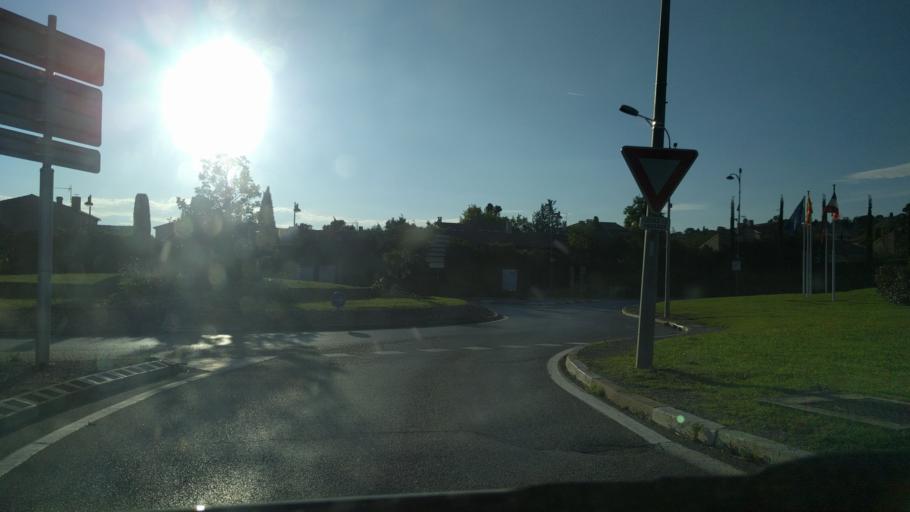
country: FR
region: Provence-Alpes-Cote d'Azur
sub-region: Departement des Bouches-du-Rhone
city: Venelles
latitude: 43.5938
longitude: 5.4828
